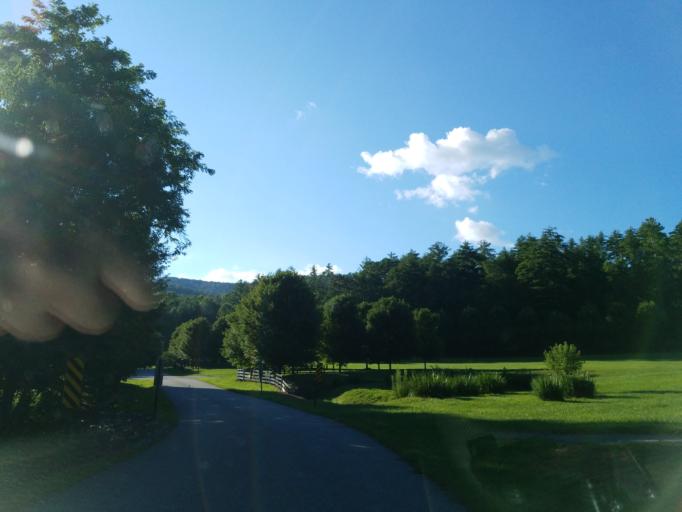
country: US
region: Georgia
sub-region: Union County
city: Blairsville
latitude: 34.7612
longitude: -84.1040
